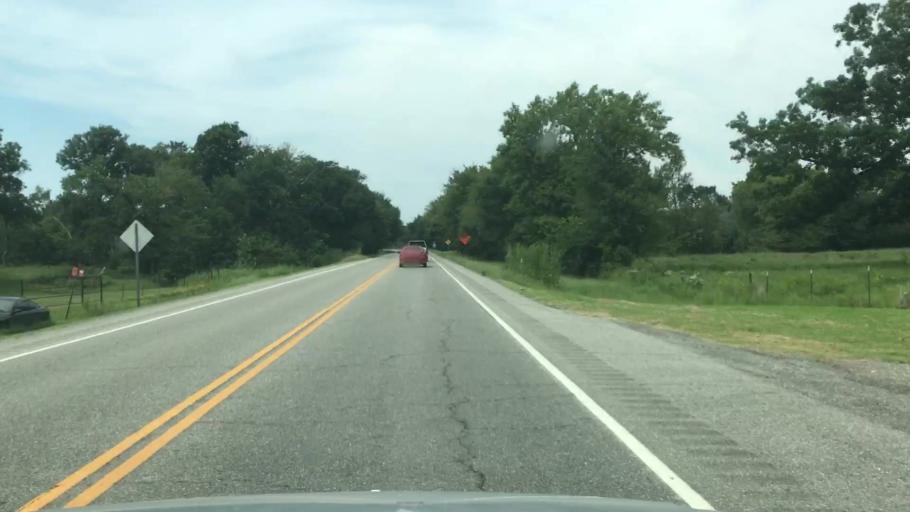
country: US
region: Oklahoma
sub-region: Muskogee County
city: Fort Gibson
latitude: 35.9349
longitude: -95.1594
